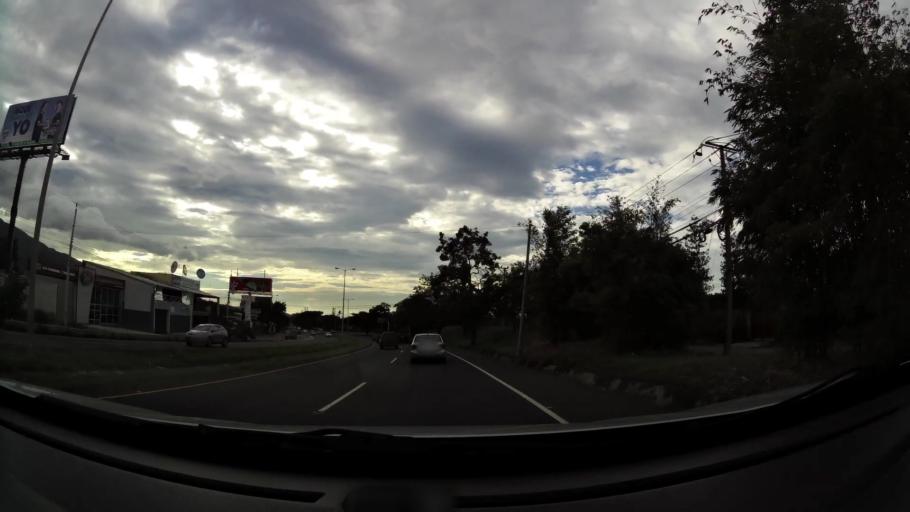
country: CR
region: San Jose
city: Santa Ana
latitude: 9.9468
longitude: -84.1843
